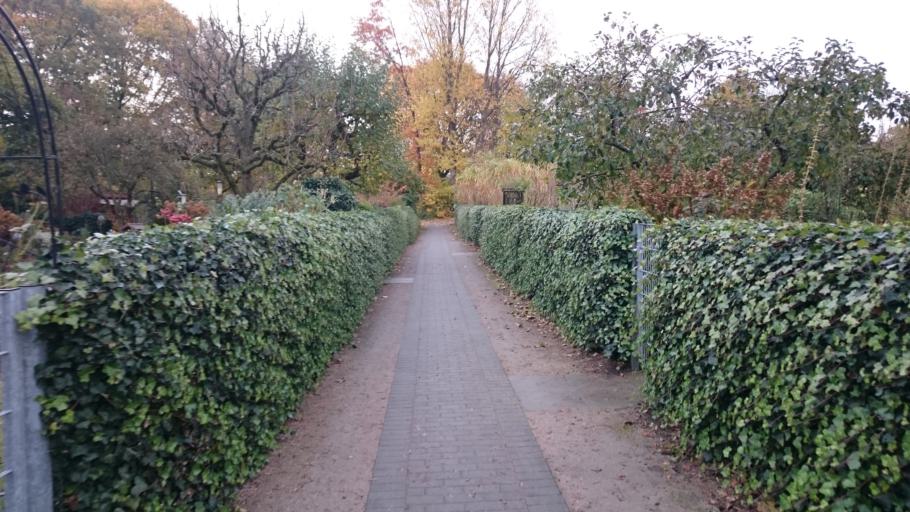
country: DE
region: Hamburg
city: Stellingen
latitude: 53.5877
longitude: 9.9458
